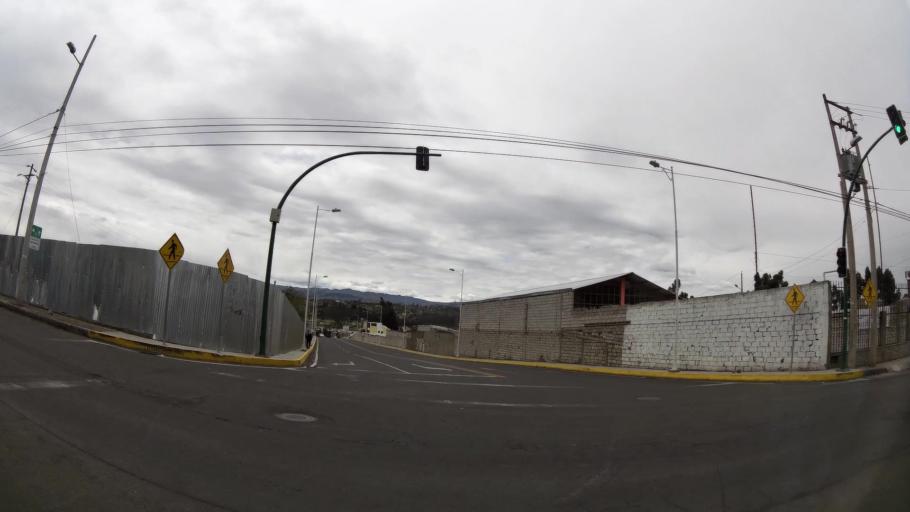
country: EC
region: Cotopaxi
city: Latacunga
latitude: -0.9498
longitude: -78.6104
